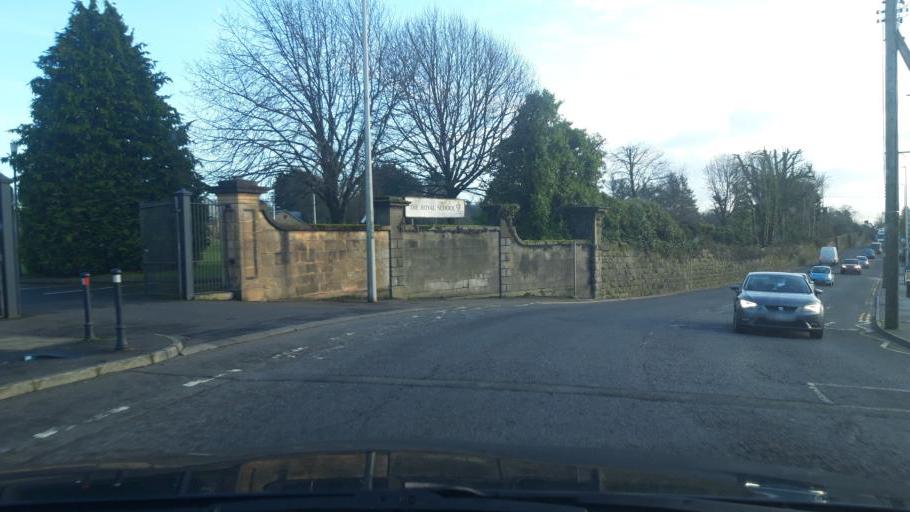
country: GB
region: Northern Ireland
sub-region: Dungannon District
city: Dungannon
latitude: 54.5029
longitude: -6.7643
